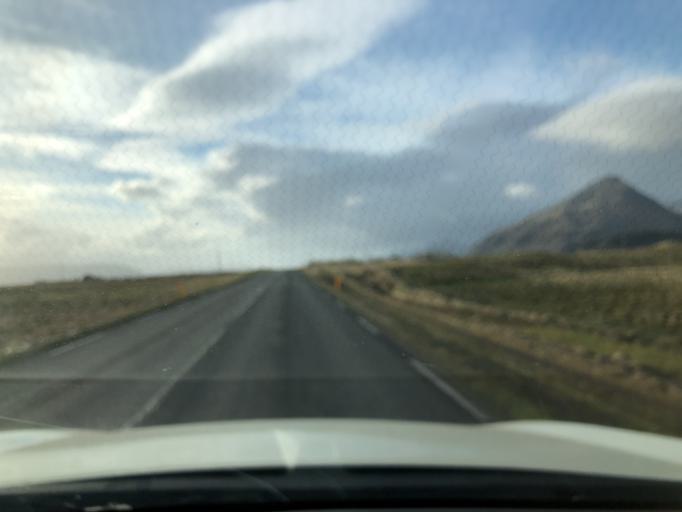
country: IS
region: East
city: Hoefn
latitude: 64.2991
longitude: -15.1981
